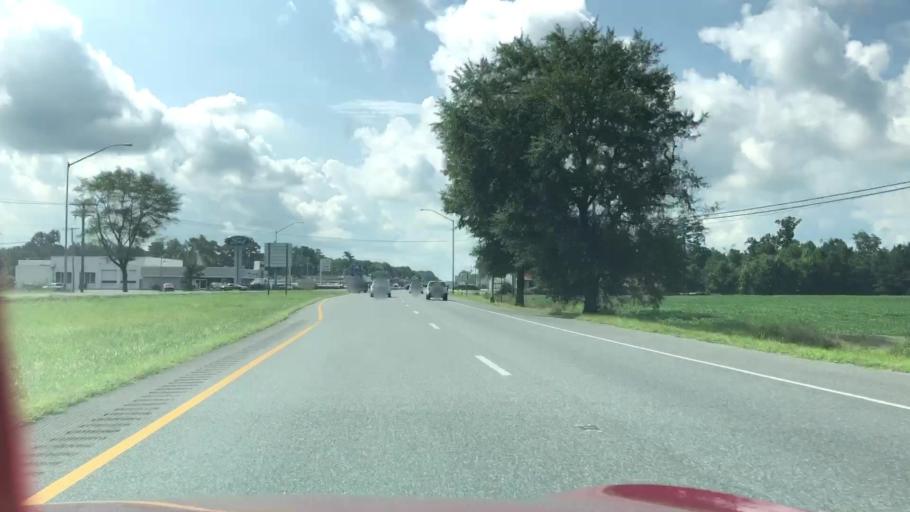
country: US
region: Maryland
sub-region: Worcester County
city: Pocomoke City
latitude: 38.0555
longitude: -75.5440
